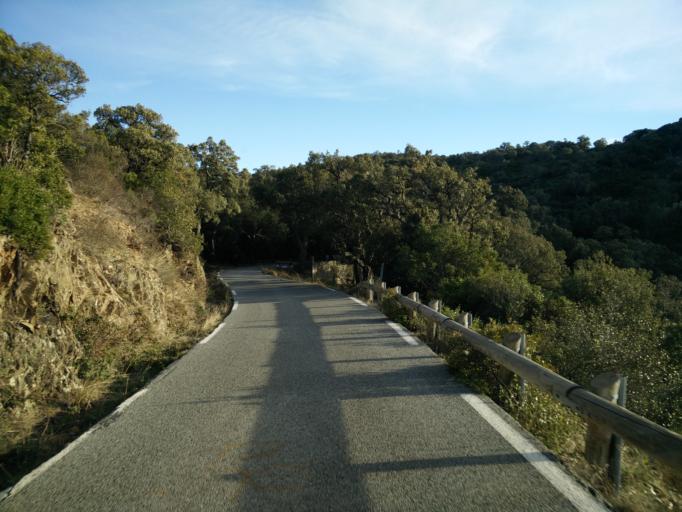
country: FR
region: Provence-Alpes-Cote d'Azur
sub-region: Departement du Var
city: Bormes-les-Mimosas
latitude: 43.1886
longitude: 6.3237
